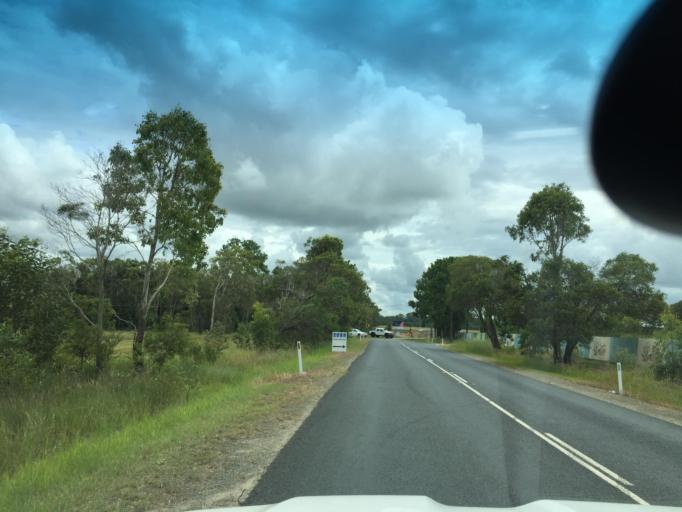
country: AU
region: Queensland
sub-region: Moreton Bay
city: Morayfield
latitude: -27.1110
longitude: 152.9804
